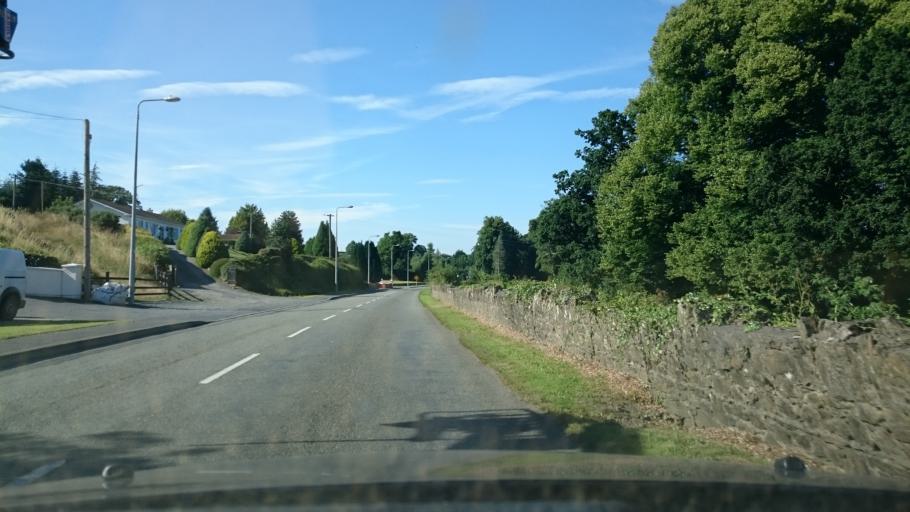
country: IE
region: Leinster
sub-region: Kilkenny
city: Graiguenamanagh
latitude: 52.5348
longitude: -6.9619
